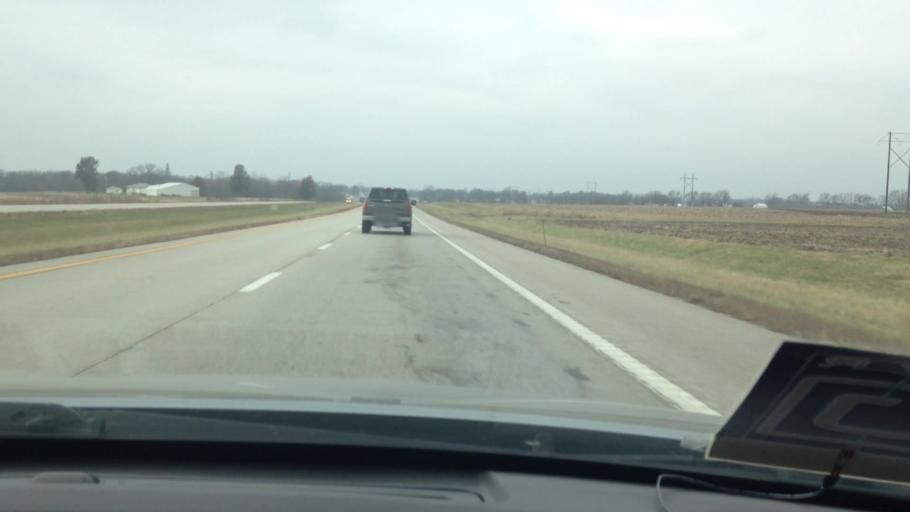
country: US
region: Missouri
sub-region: Cass County
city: Garden City
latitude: 38.5883
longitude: -94.2335
